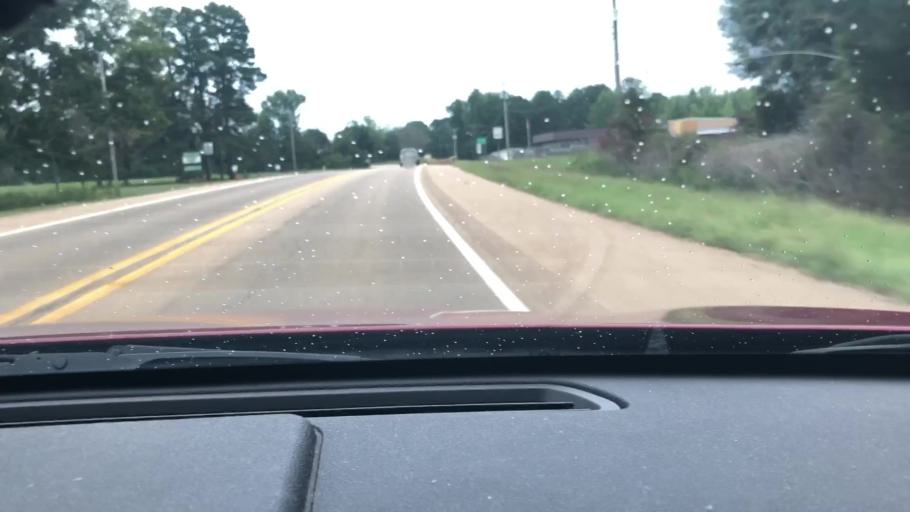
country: US
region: Arkansas
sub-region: Lafayette County
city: Stamps
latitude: 33.3671
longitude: -93.5128
